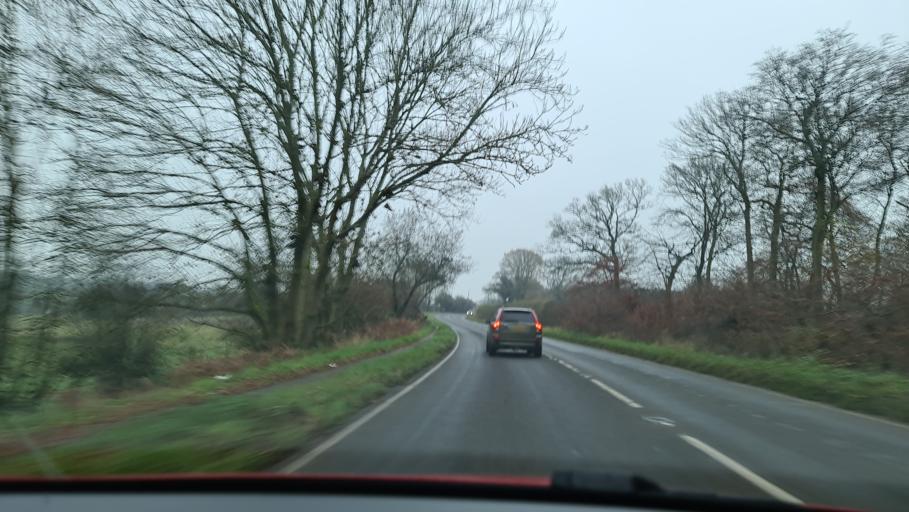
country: GB
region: England
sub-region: Buckinghamshire
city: Stokenchurch
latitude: 51.6526
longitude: -0.8720
